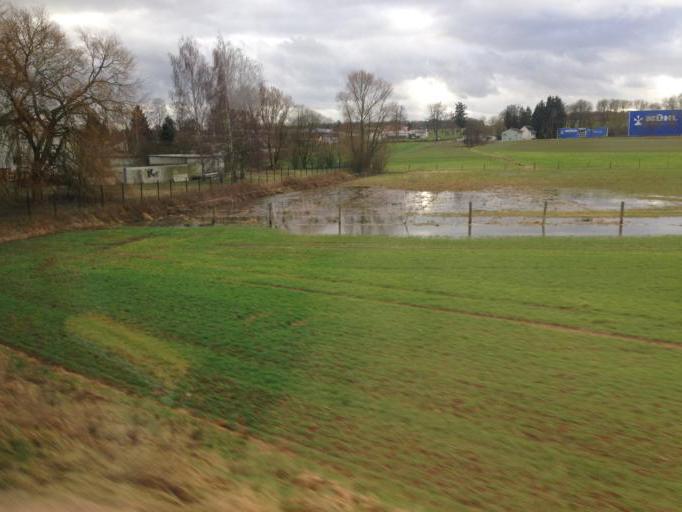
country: DE
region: Hesse
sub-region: Regierungsbezirk Giessen
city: Hungen
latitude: 50.4808
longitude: 8.8843
